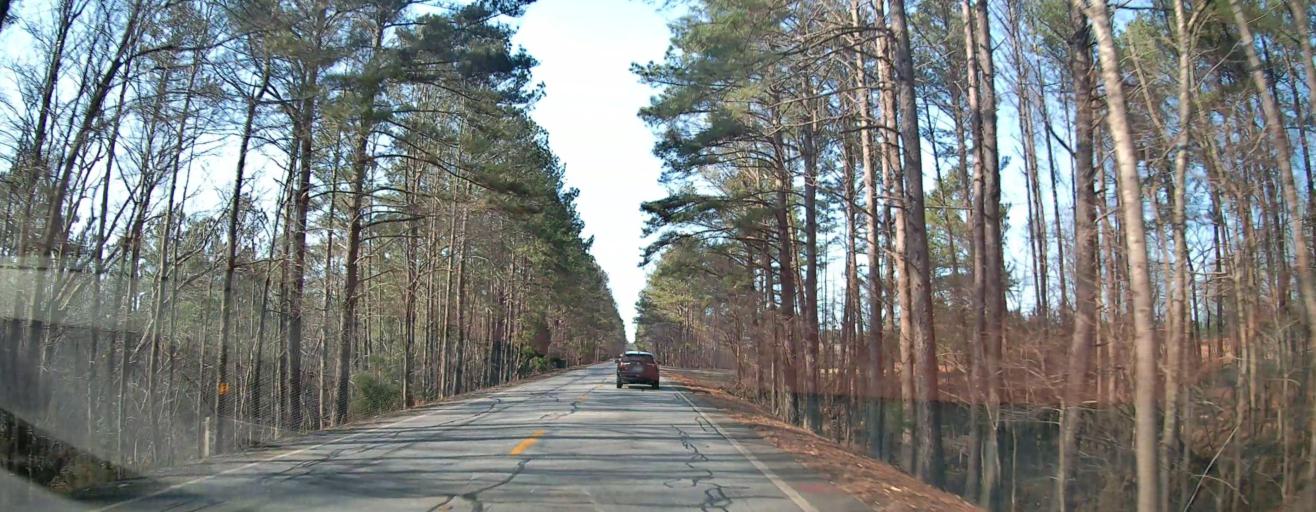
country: US
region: Georgia
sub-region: Butts County
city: Indian Springs
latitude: 33.2191
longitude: -83.8671
